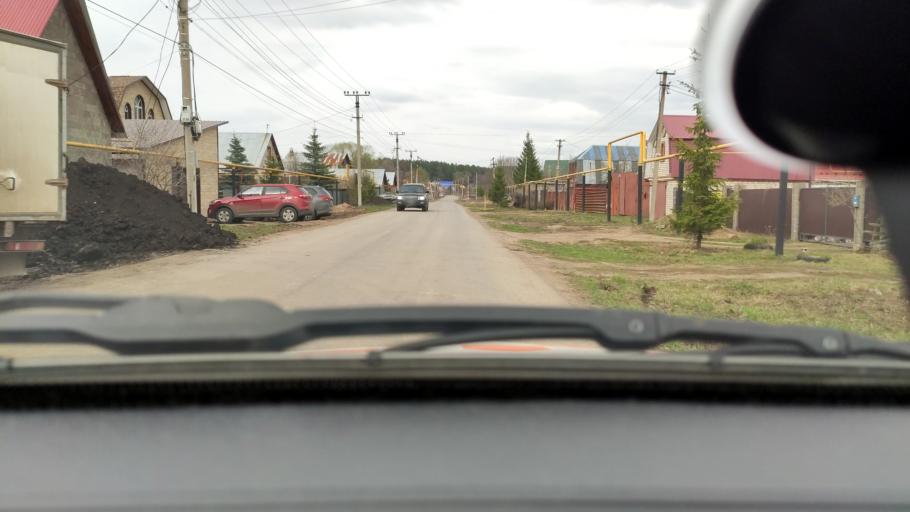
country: RU
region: Bashkortostan
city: Iglino
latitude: 54.8397
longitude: 56.2084
